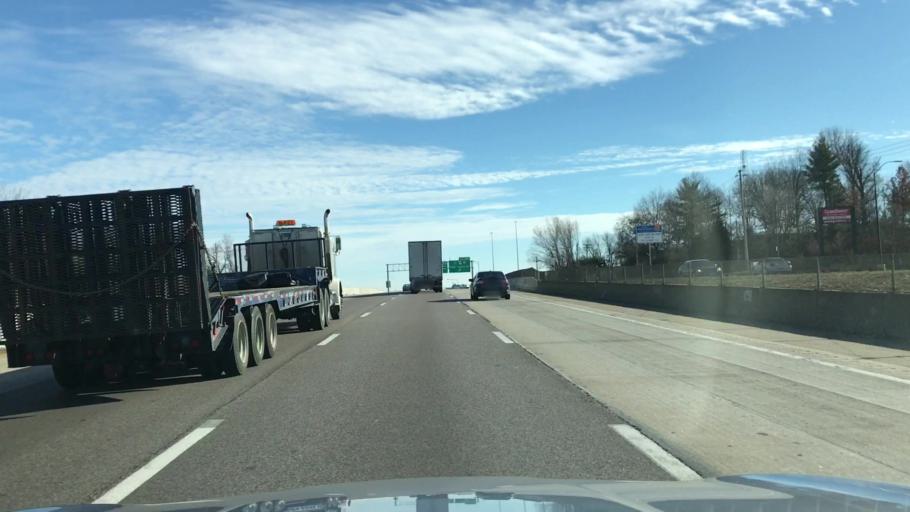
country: US
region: Missouri
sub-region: Saint Charles County
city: Saint Charles
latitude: 38.7801
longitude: -90.5168
